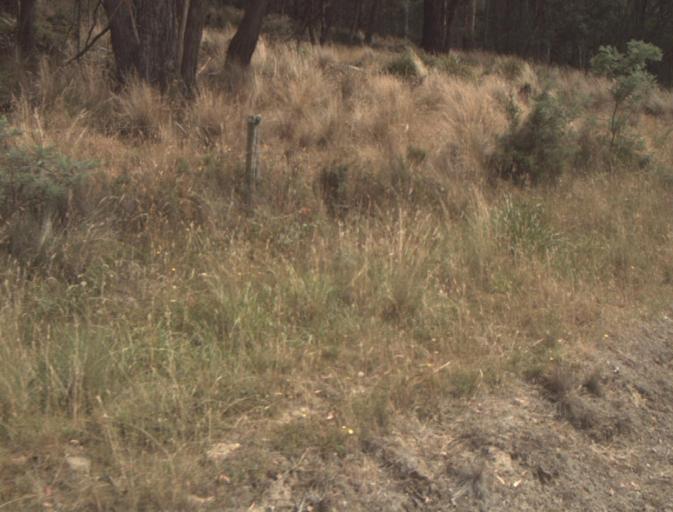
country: AU
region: Tasmania
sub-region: Northern Midlands
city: Evandale
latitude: -41.4811
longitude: 147.4421
